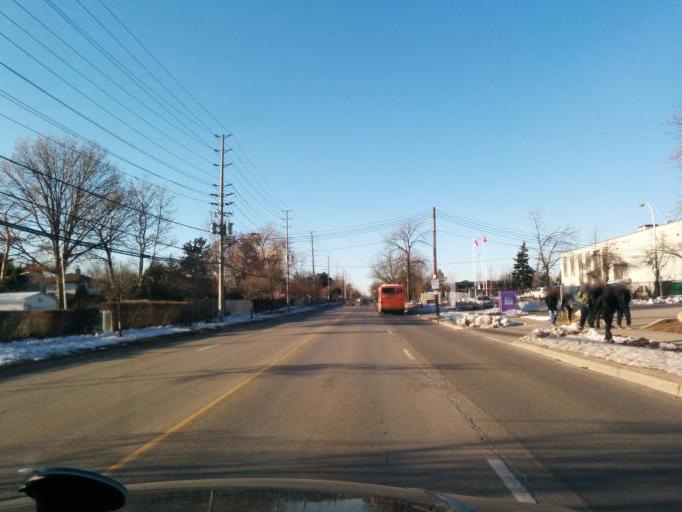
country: CA
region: Ontario
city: Mississauga
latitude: 43.5609
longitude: -79.6478
